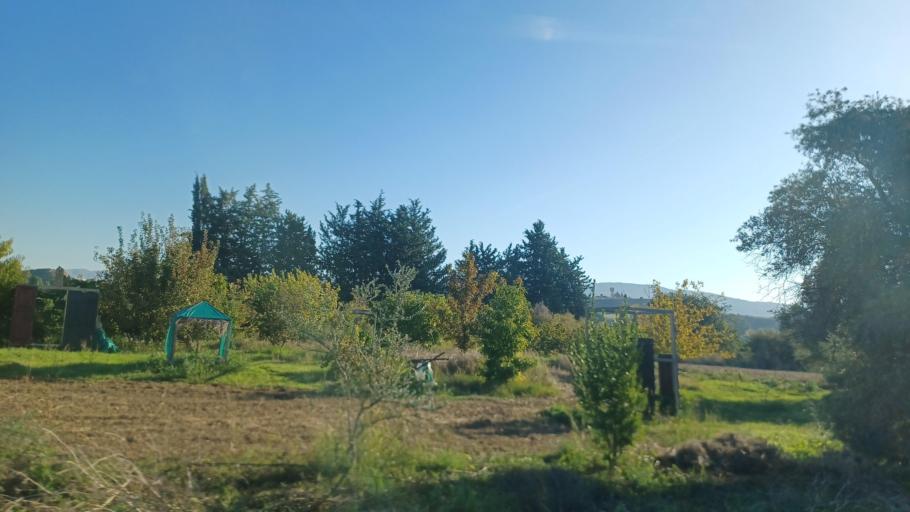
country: CY
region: Pafos
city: Polis
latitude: 35.0148
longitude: 32.4287
